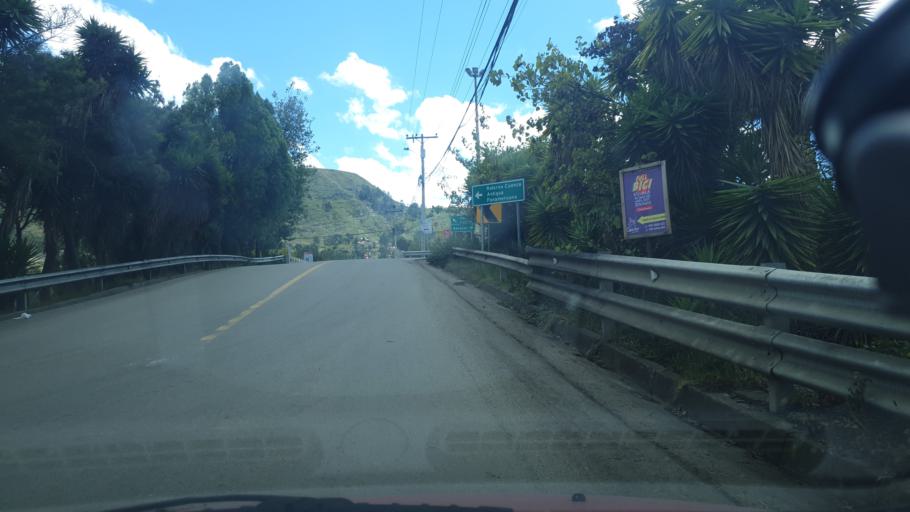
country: EC
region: Azuay
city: Llacao
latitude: -2.8540
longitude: -78.9102
